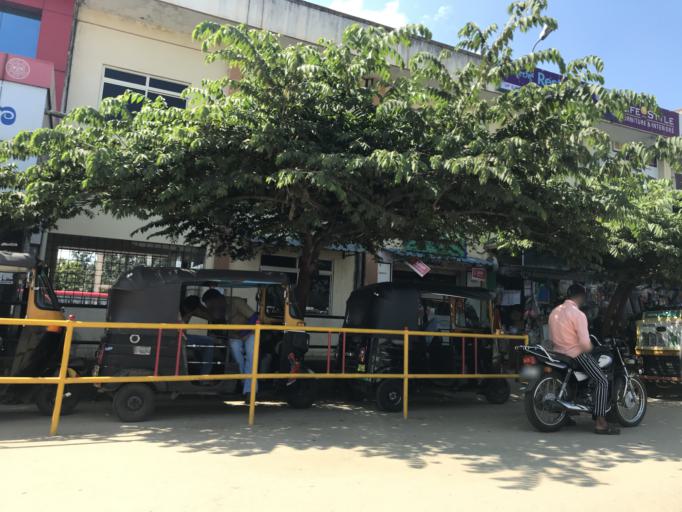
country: IN
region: Karnataka
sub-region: Mysore
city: Heggadadevankote
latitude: 12.0863
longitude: 76.3323
